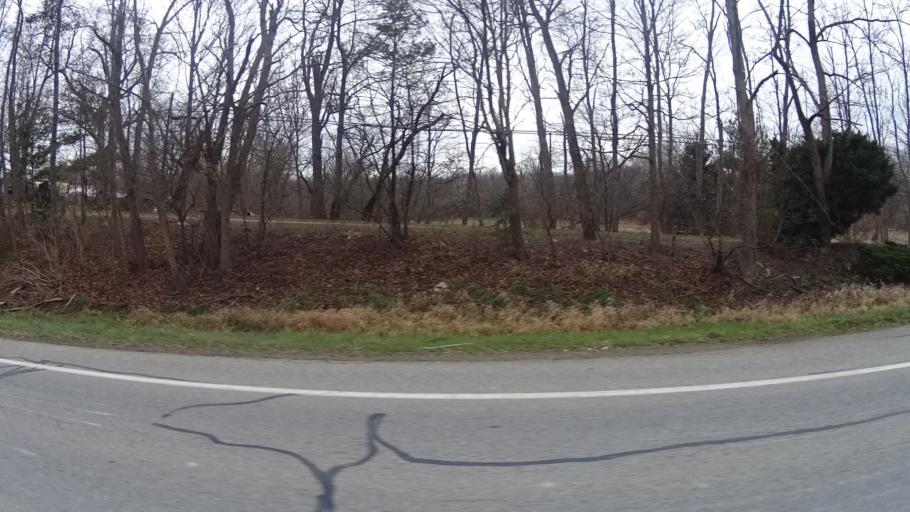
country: US
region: Ohio
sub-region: Lorain County
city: Camden
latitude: 41.1704
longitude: -82.2883
